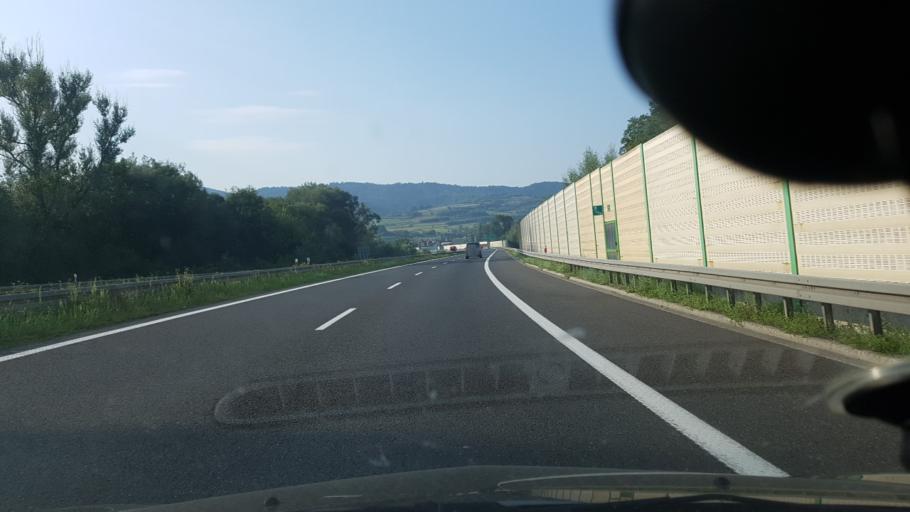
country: PL
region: Lesser Poland Voivodeship
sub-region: Powiat myslenicki
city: Lubien
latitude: 49.7259
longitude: 19.9790
